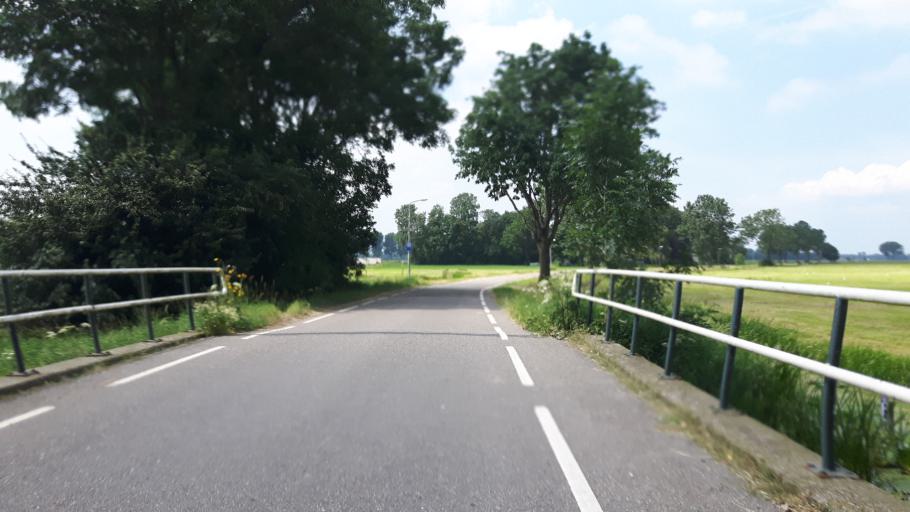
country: NL
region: Utrecht
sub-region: Gemeente Lopik
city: Lopik
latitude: 51.9202
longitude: 4.9648
